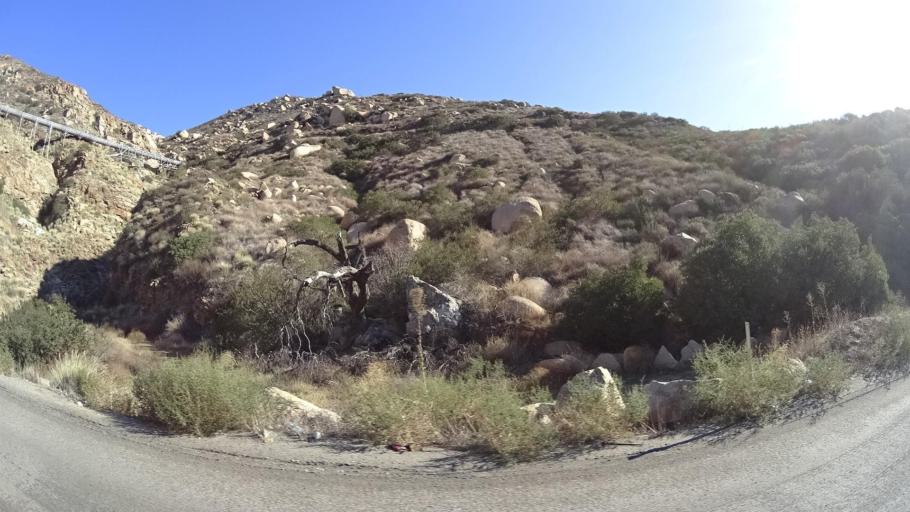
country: MX
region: Baja California
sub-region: Tecate
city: Lomas de Santa Anita
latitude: 32.6188
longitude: -116.7276
